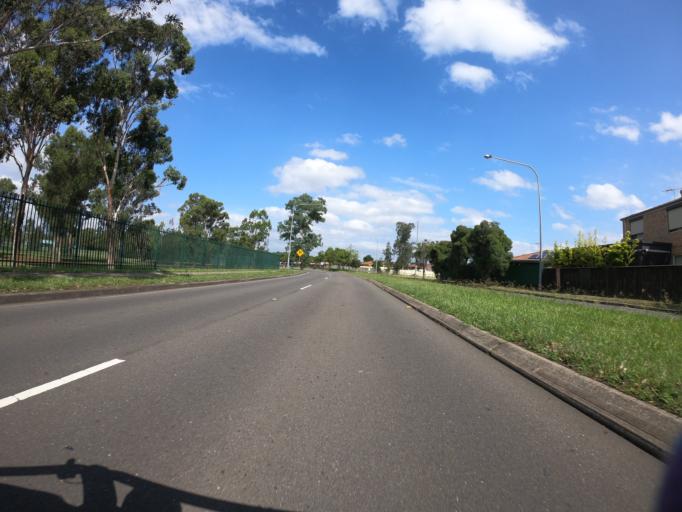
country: AU
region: New South Wales
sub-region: Blacktown
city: Hassall Grove
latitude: -33.7365
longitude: 150.8379
